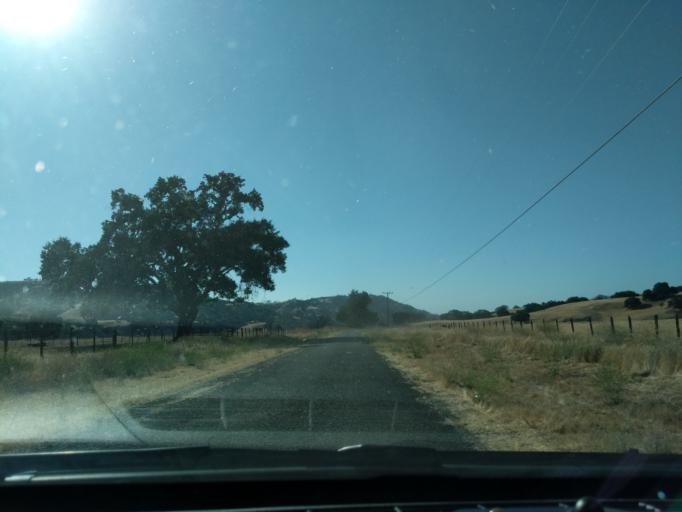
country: US
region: California
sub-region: San Luis Obispo County
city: San Miguel
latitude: 36.1144
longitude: -120.7242
